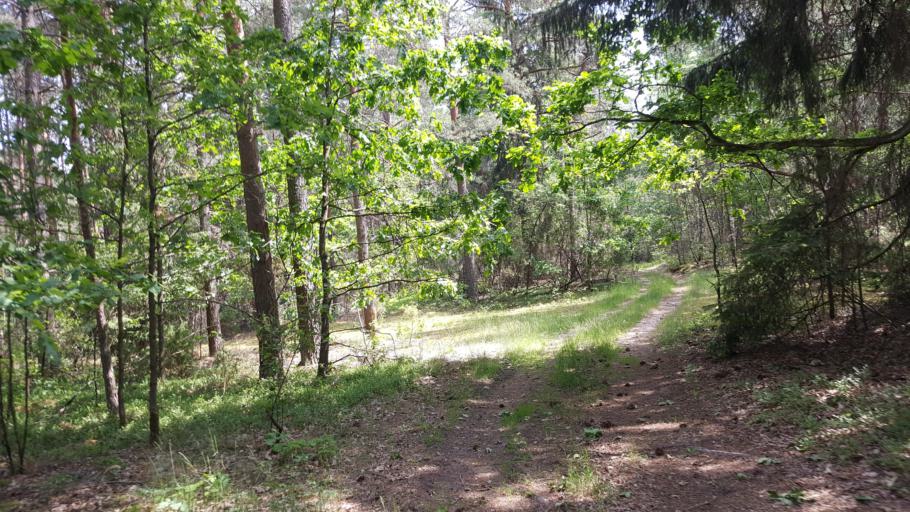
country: BY
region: Brest
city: Kamyanyuki
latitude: 52.5038
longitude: 23.8334
